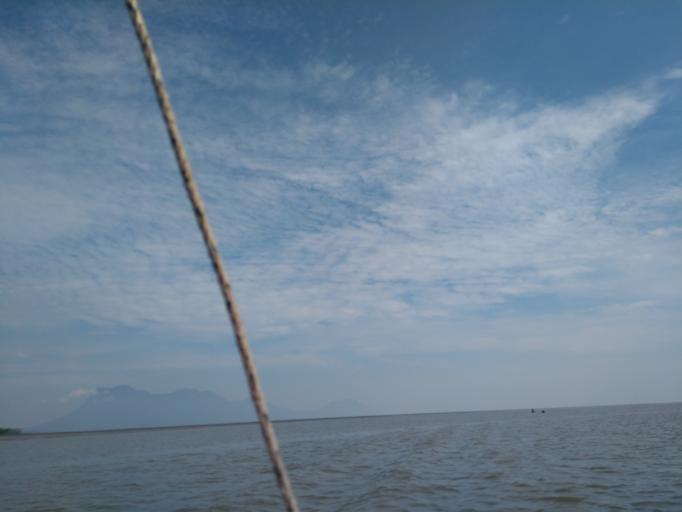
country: MY
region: Sarawak
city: Kuching
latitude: 1.6800
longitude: 110.4246
